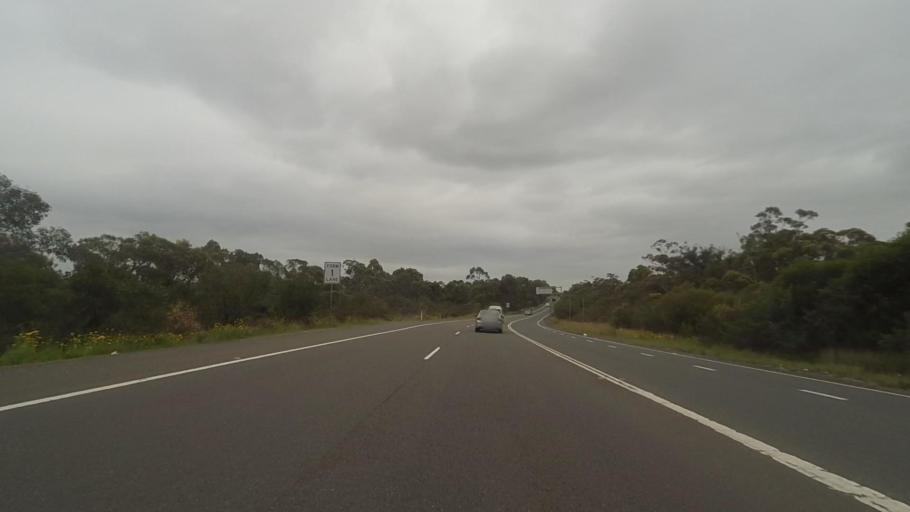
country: AU
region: New South Wales
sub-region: Sutherland Shire
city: Engadine
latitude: -34.0532
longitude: 150.9716
